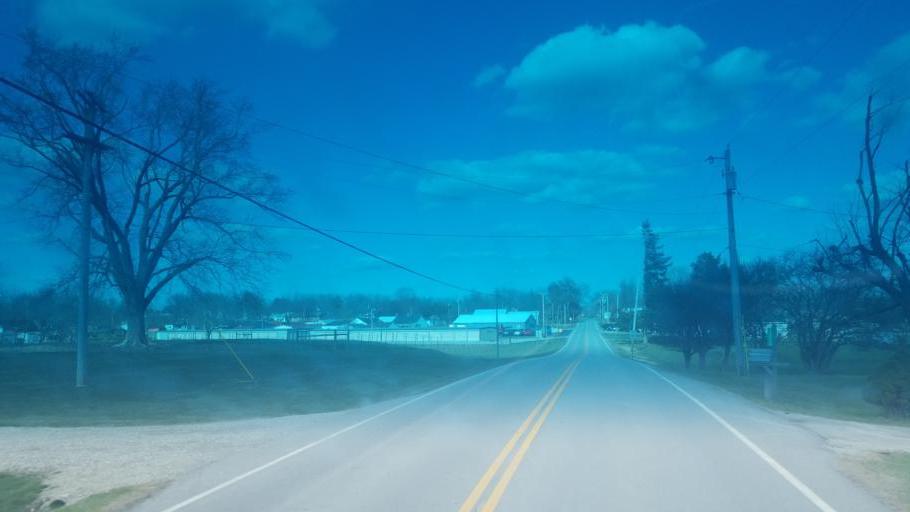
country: US
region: Ohio
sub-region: Highland County
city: Greenfield
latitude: 39.3419
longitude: -83.3977
